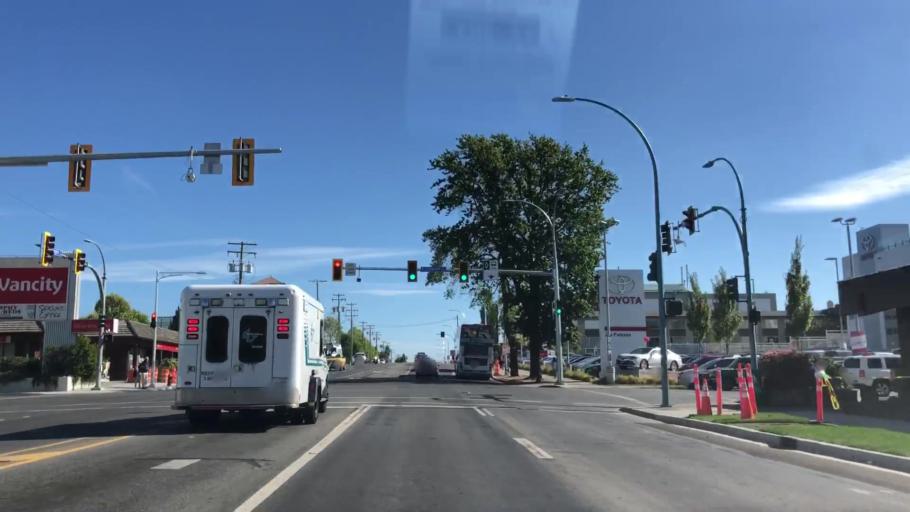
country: CA
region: British Columbia
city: Victoria
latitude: 48.4453
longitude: -123.3709
